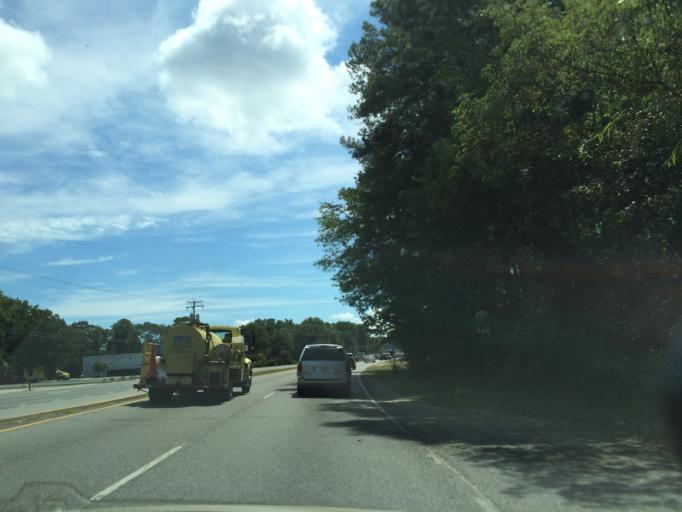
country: US
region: Virginia
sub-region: York County
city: Yorktown
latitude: 37.1973
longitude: -76.4923
